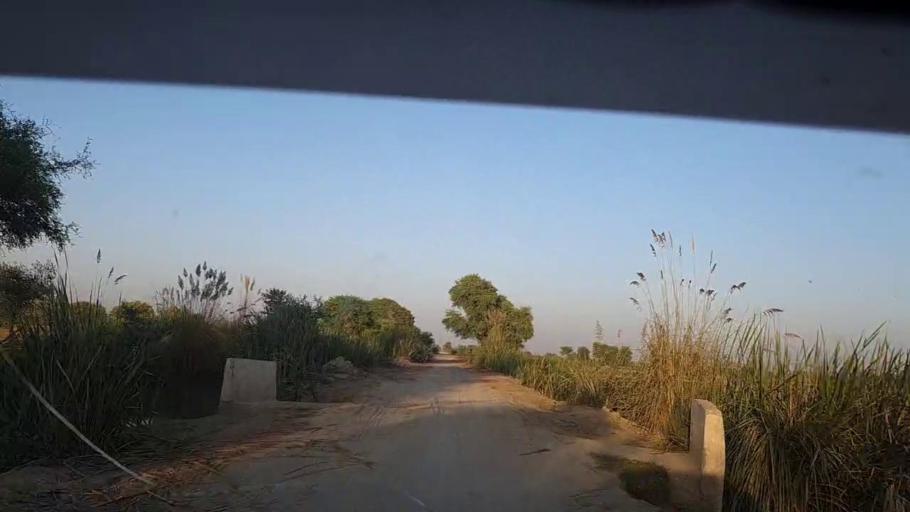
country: PK
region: Sindh
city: Ratodero
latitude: 27.8832
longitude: 68.2094
